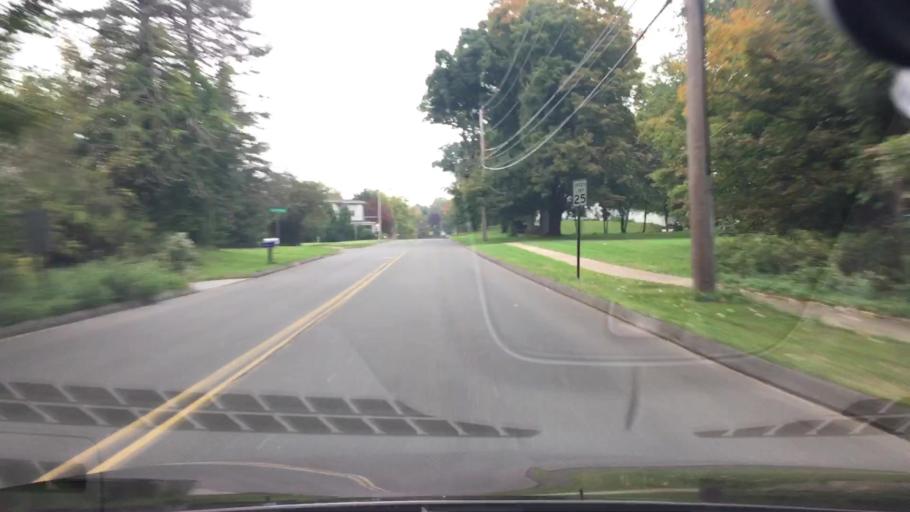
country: US
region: Connecticut
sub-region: Hartford County
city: Kensington
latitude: 41.6065
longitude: -72.7193
